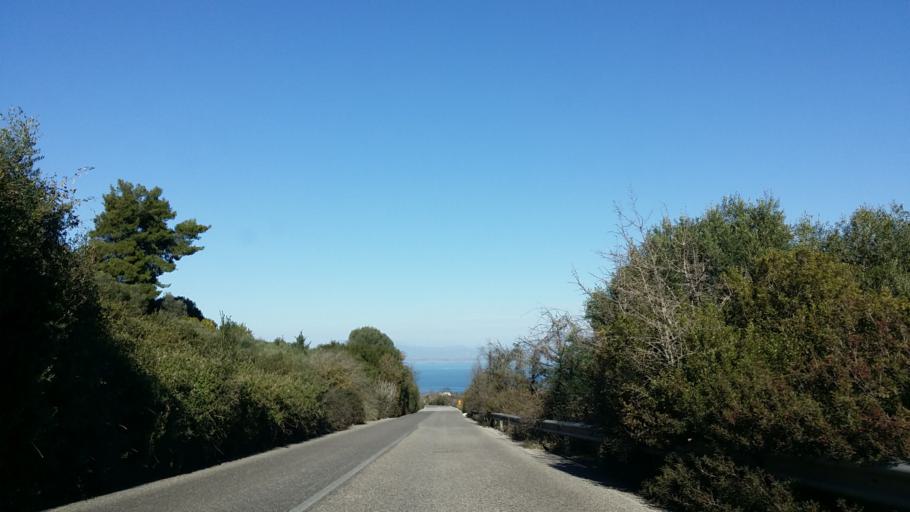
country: GR
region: West Greece
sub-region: Nomos Aitolias kai Akarnanias
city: Vonitsa
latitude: 38.9136
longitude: 20.9471
